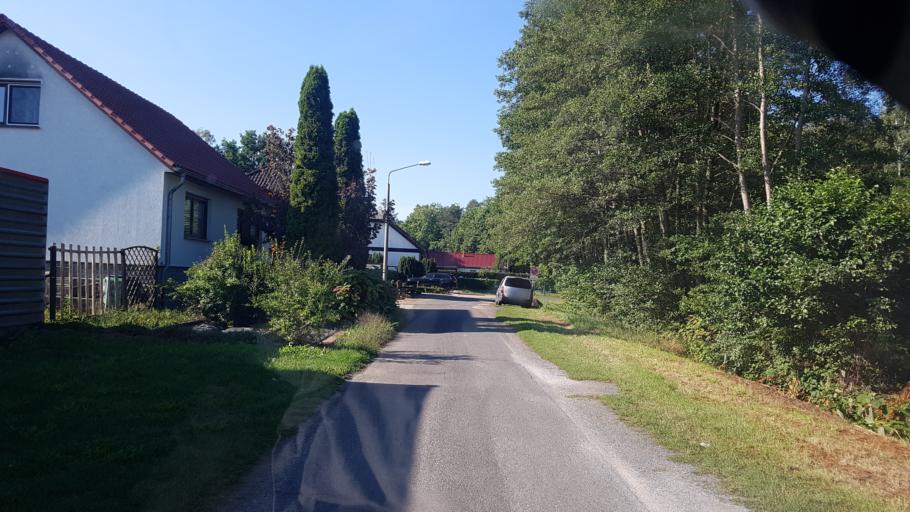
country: DE
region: Brandenburg
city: Calau
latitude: 51.7420
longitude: 13.9744
